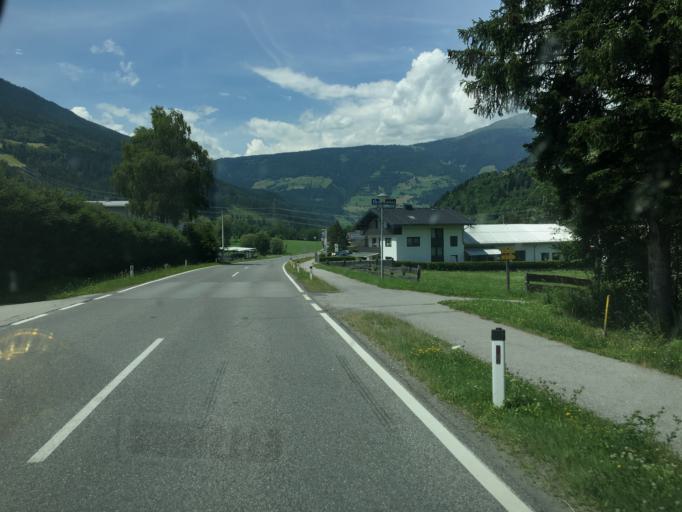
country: AT
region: Carinthia
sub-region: Politischer Bezirk Spittal an der Drau
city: Rangersdorf
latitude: 46.8540
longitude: 12.9268
